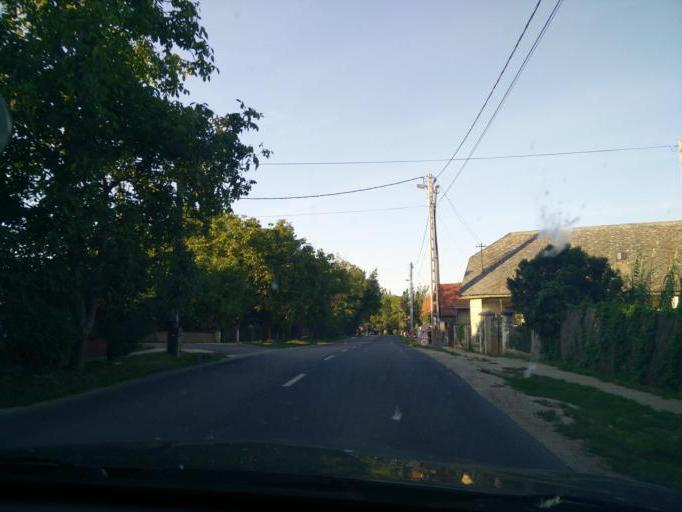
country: HU
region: Pest
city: Zsambek
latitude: 47.5643
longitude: 18.7311
